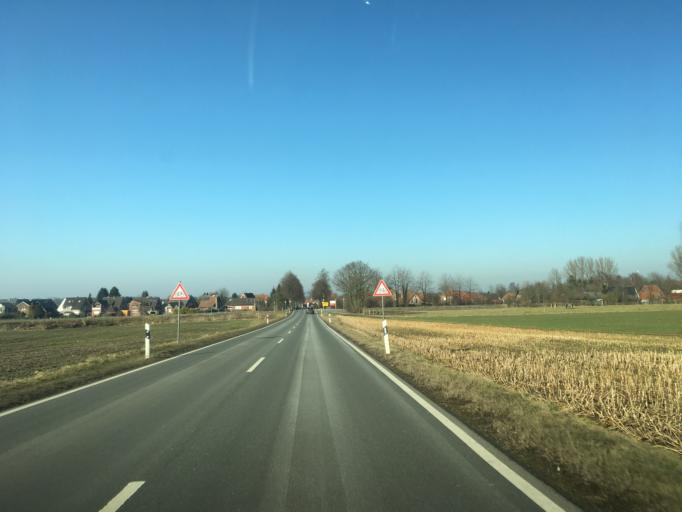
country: DE
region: North Rhine-Westphalia
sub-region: Regierungsbezirk Munster
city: Billerbeck
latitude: 52.0180
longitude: 7.2760
